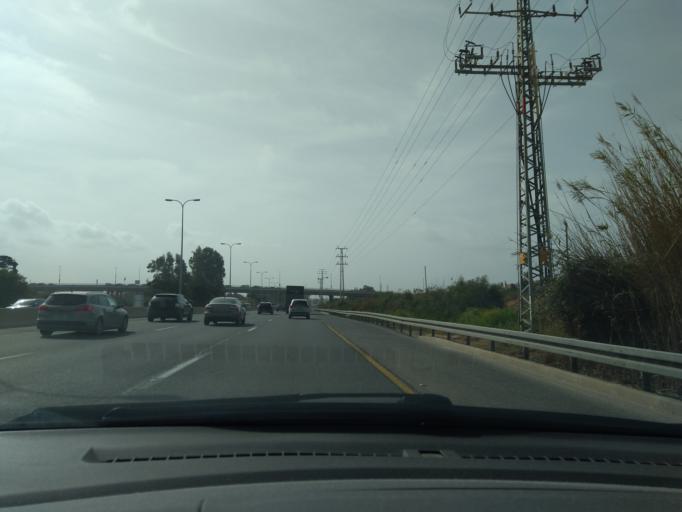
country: IL
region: Central District
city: Netanya
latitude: 32.3148
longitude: 34.8657
